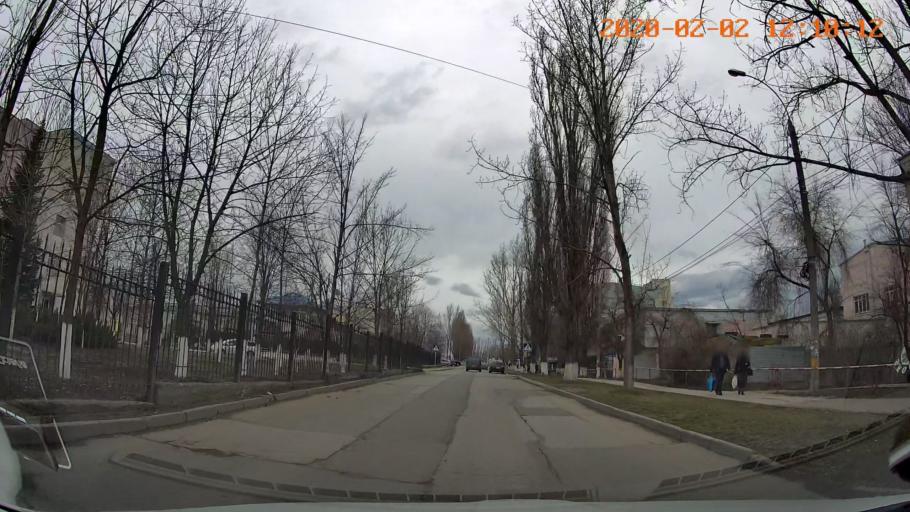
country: MD
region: Chisinau
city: Chisinau
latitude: 46.9991
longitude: 28.8048
